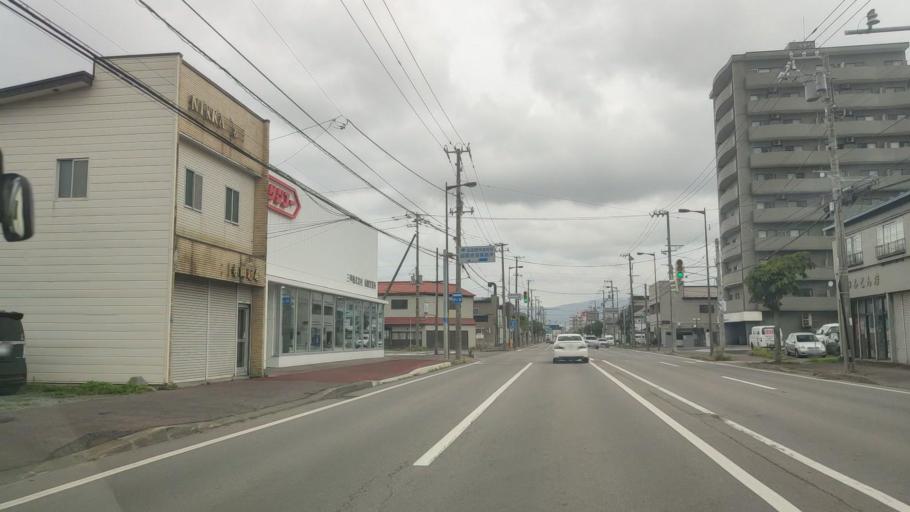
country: JP
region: Hokkaido
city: Hakodate
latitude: 41.7826
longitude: 140.7301
